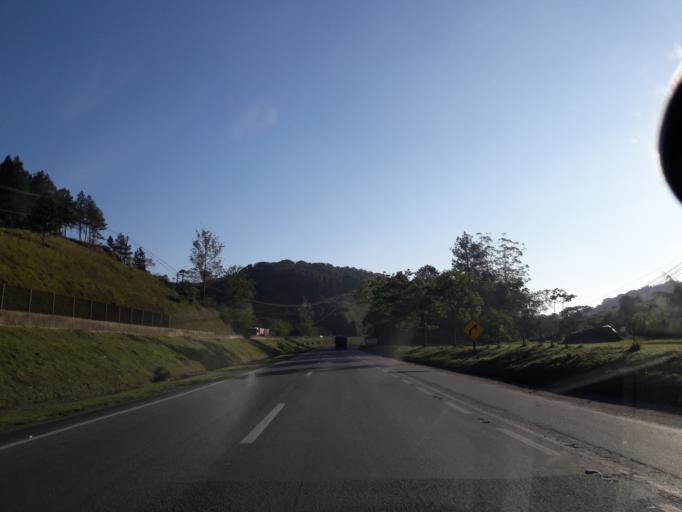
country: BR
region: Sao Paulo
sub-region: Juquitiba
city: Juquitiba
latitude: -23.9390
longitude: -47.0401
